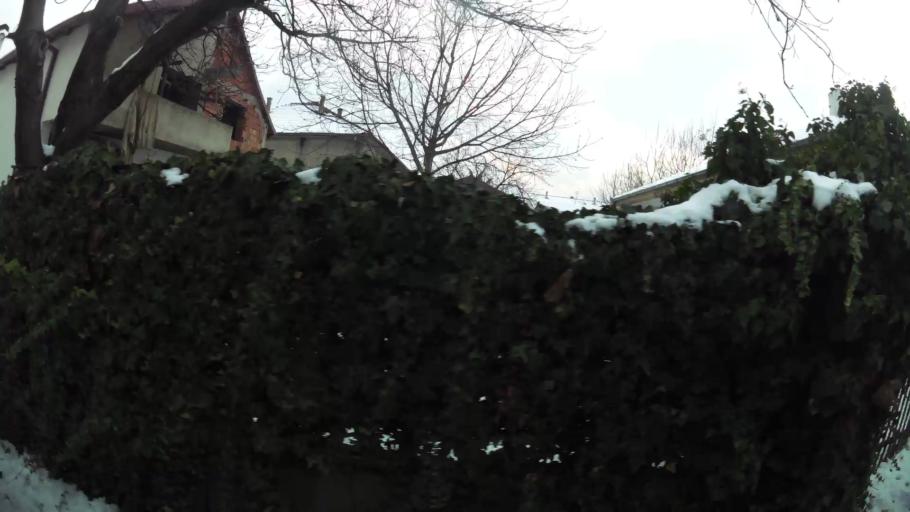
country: MK
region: Saraj
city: Saraj
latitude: 42.0242
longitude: 21.3526
